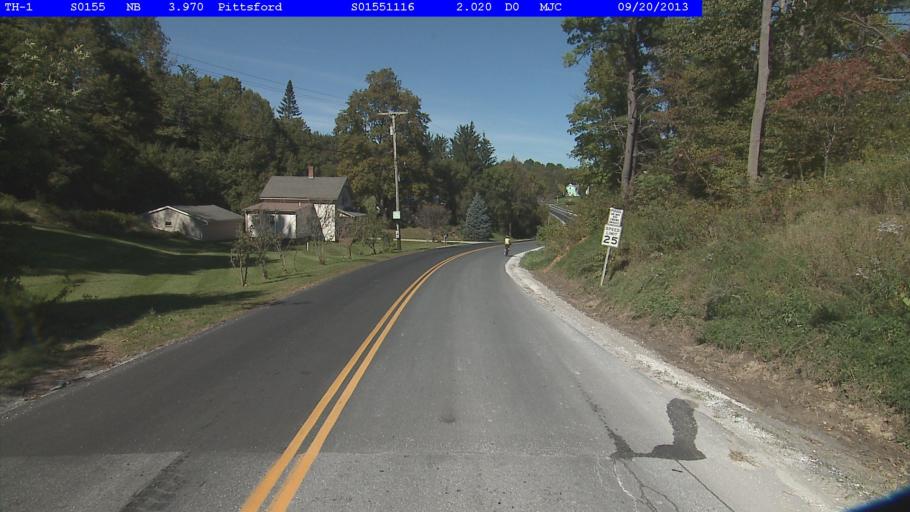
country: US
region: Vermont
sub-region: Rutland County
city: Brandon
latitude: 43.7169
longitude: -73.0606
